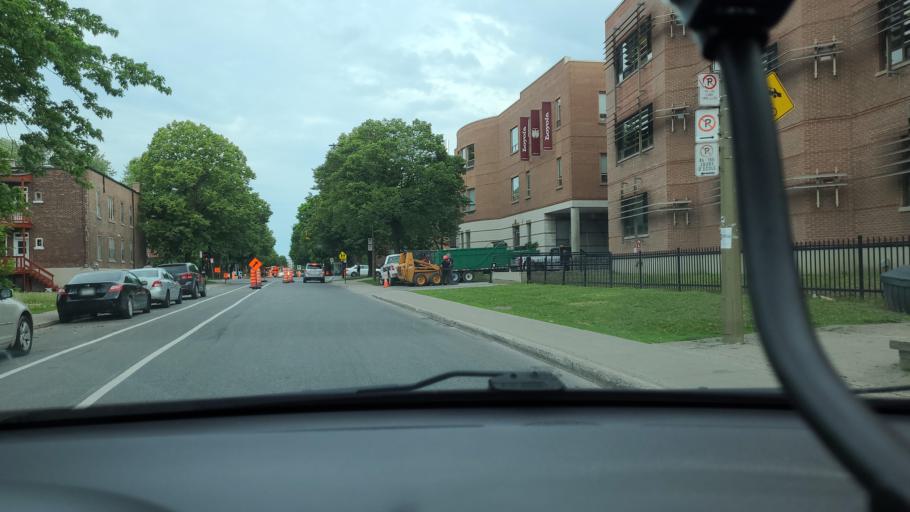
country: CA
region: Quebec
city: Montreal-Ouest
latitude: 45.4562
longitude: -73.6392
